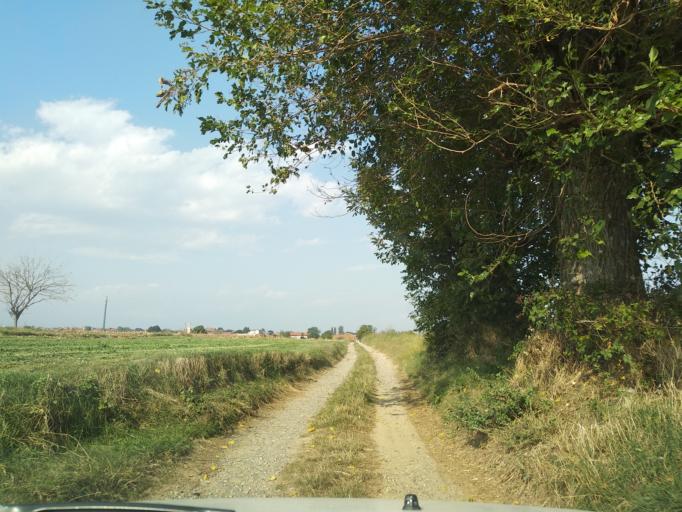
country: IT
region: Piedmont
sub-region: Provincia di Torino
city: Tetti Neirotti
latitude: 45.0440
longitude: 7.5418
